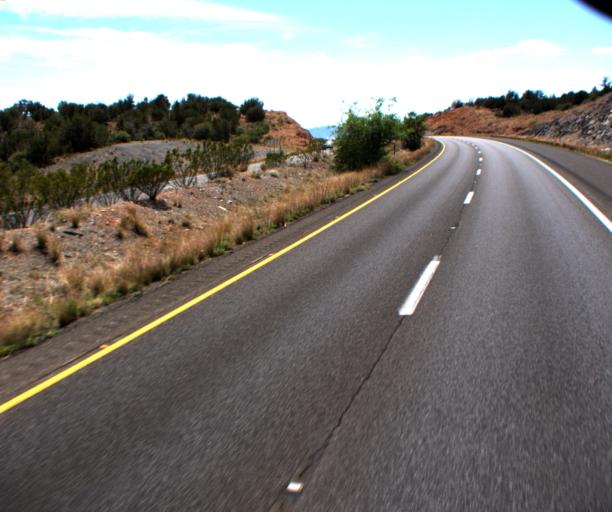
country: US
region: Arizona
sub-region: Yavapai County
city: West Sedona
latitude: 34.8374
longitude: -111.8878
